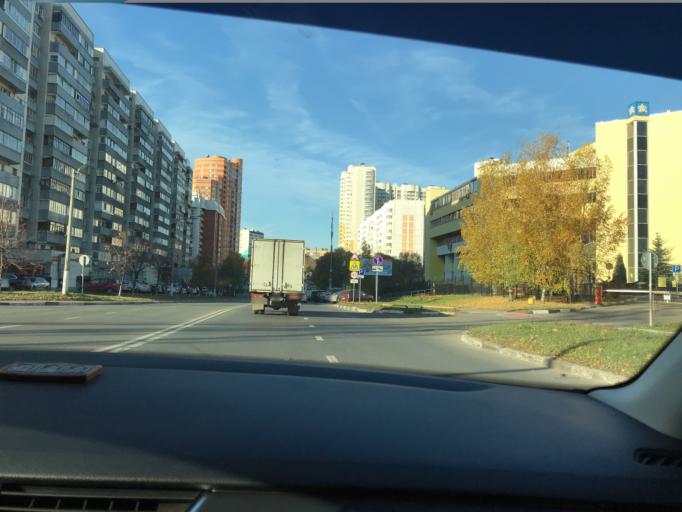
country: RU
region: Moscow
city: Khimki
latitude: 55.8831
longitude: 37.4287
